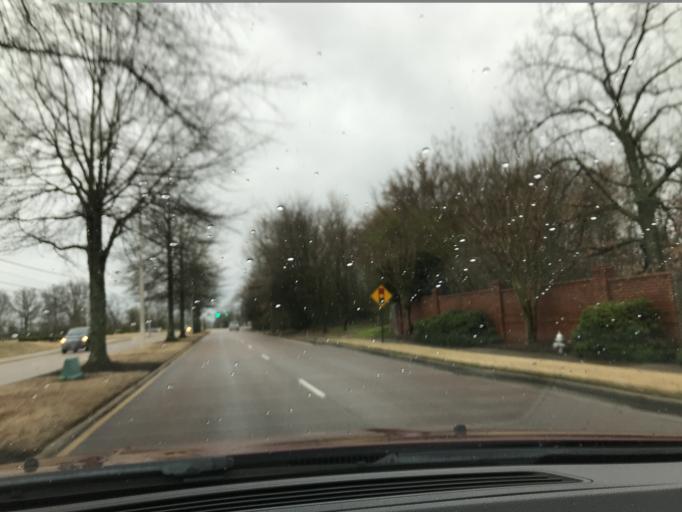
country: US
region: Tennessee
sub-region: Shelby County
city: Collierville
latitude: 35.0560
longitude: -89.6862
